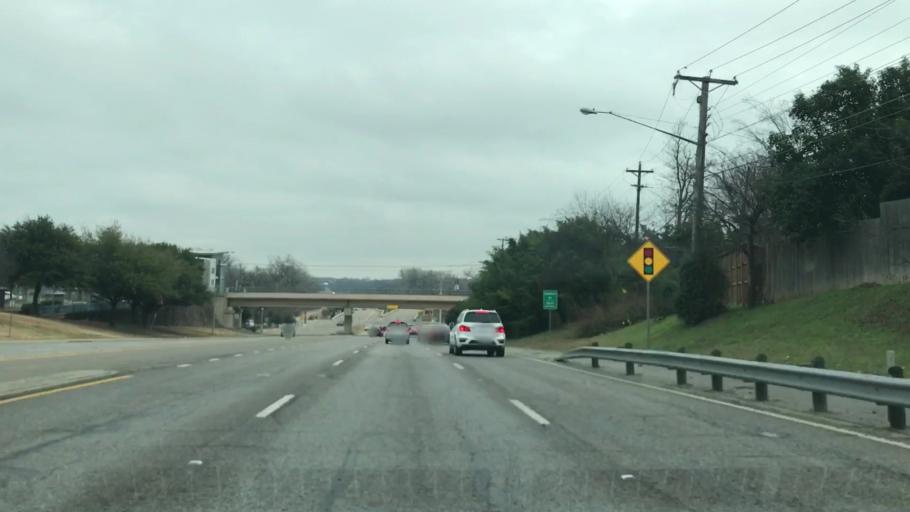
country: US
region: Texas
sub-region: Dallas County
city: Highland Park
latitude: 32.8544
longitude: -96.7342
